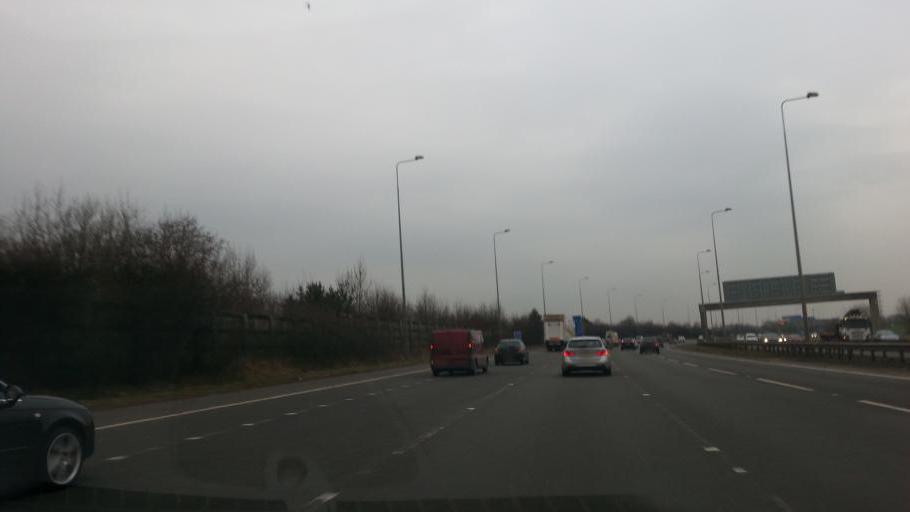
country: GB
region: England
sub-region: Borough of Tameside
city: Droylsden
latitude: 53.4635
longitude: -2.1390
